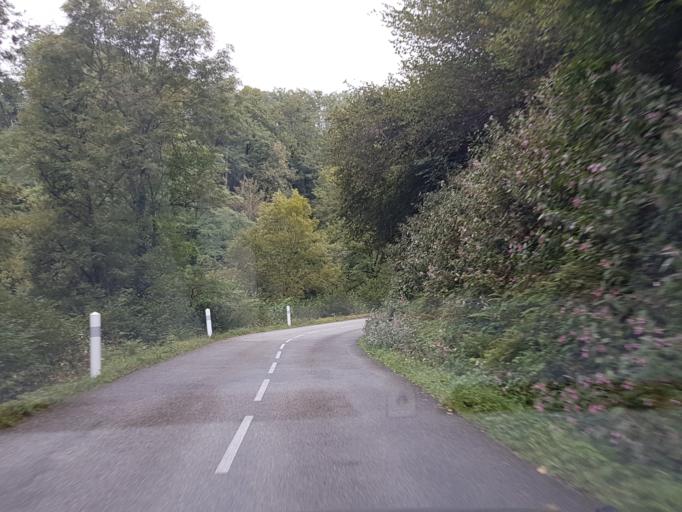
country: FR
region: Midi-Pyrenees
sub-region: Departement de l'Ariege
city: Saint-Girons
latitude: 42.9019
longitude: 1.2367
